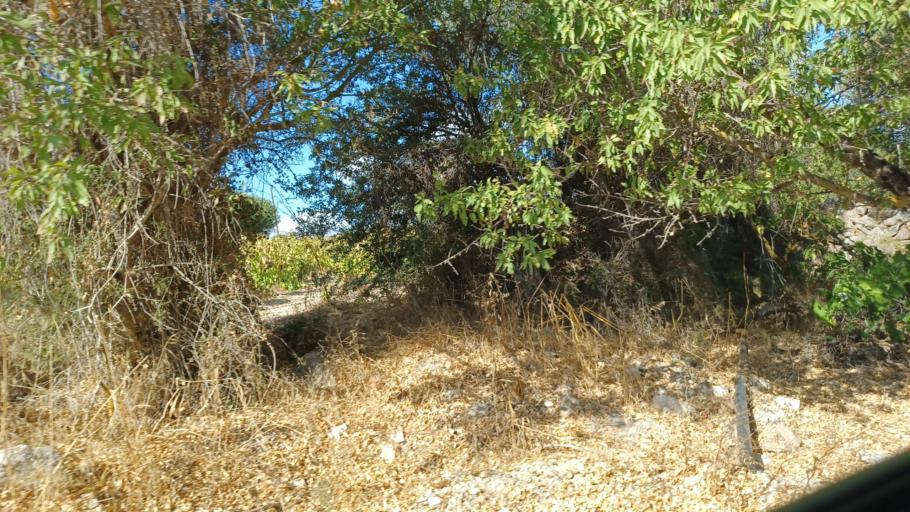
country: CY
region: Pafos
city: Mesogi
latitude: 34.8476
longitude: 32.5235
